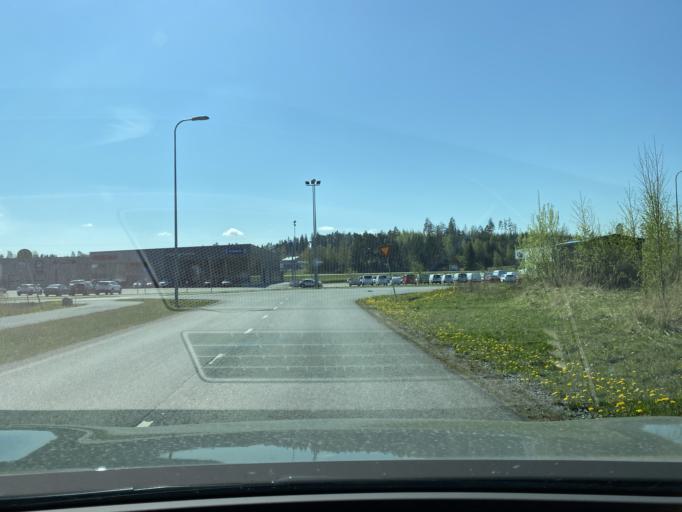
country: FI
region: Pirkanmaa
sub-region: Lounais-Pirkanmaa
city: Vammala
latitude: 61.3233
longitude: 22.9151
